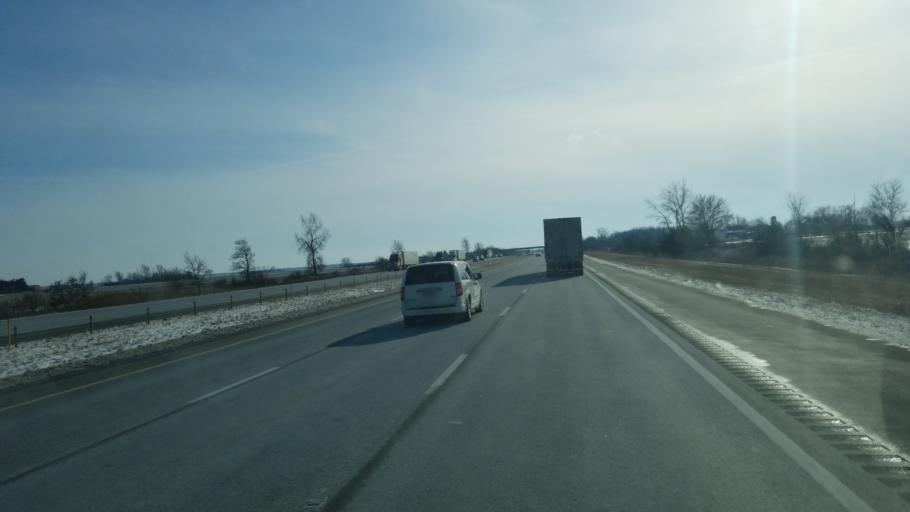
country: US
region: Ohio
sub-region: Wood County
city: Bowling Green
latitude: 41.3034
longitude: -83.6294
